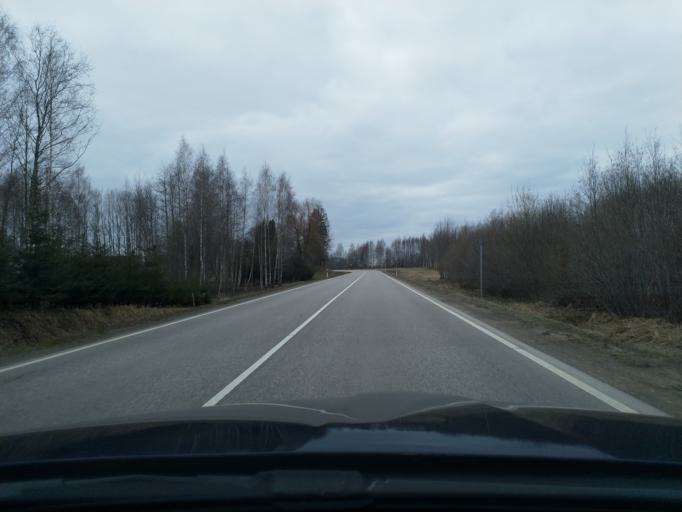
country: LV
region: Talsu Rajons
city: Sabile
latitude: 56.9481
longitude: 22.4769
